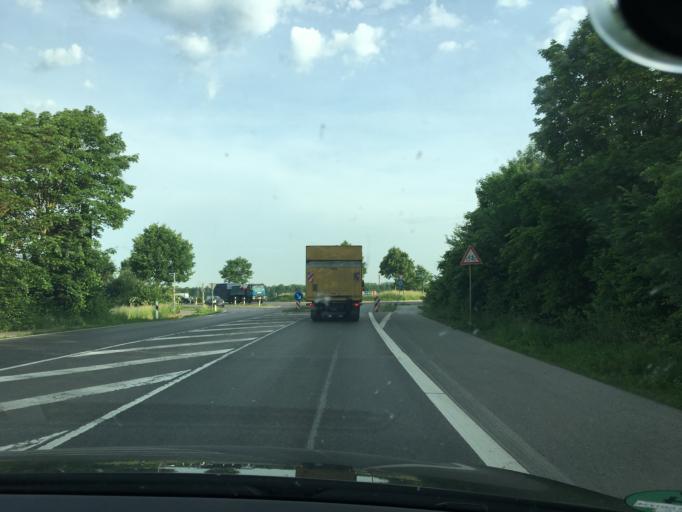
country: DE
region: North Rhine-Westphalia
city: Julich
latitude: 50.9143
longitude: 6.3377
